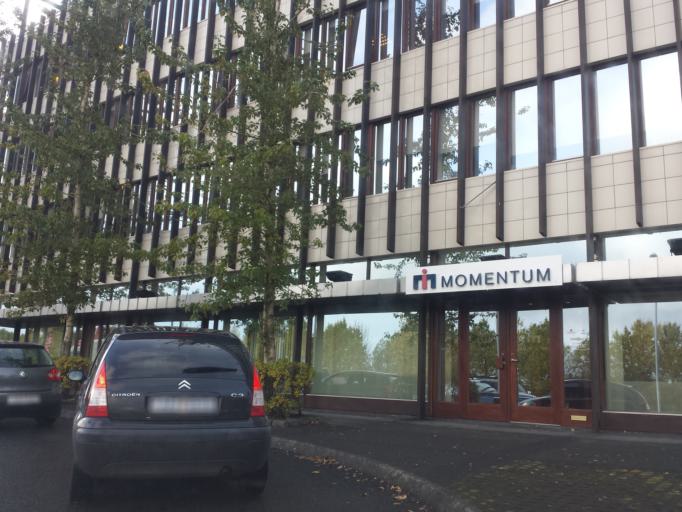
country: IS
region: Capital Region
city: Reykjavik
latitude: 64.1383
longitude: -21.8784
